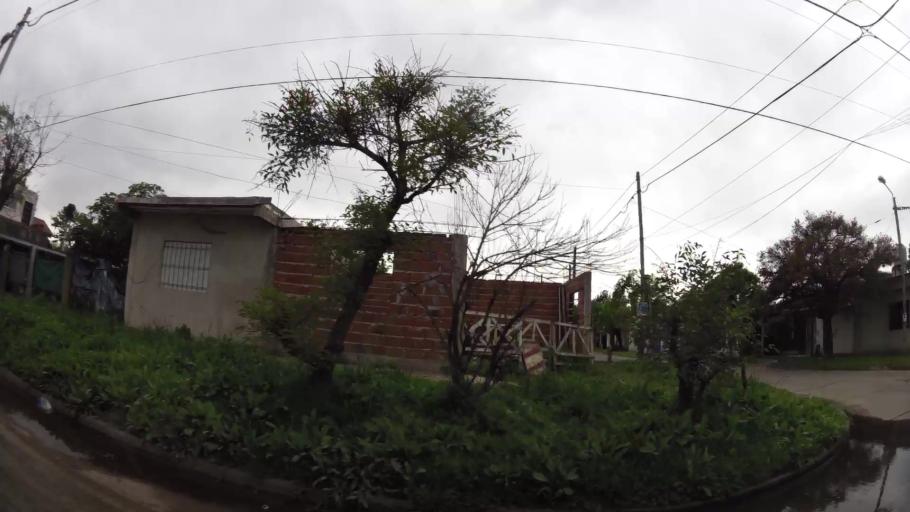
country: AR
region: Buenos Aires
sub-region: Partido de Quilmes
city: Quilmes
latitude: -34.8002
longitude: -58.2716
